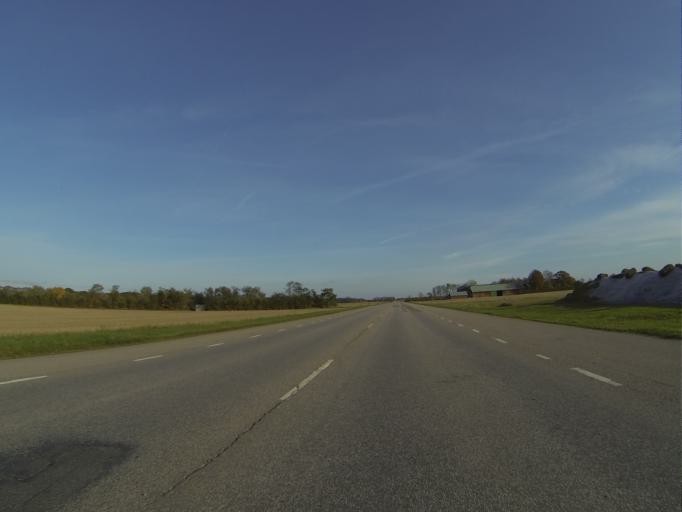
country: SE
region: Skane
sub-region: Hoors Kommun
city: Loberod
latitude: 55.7304
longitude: 13.4168
